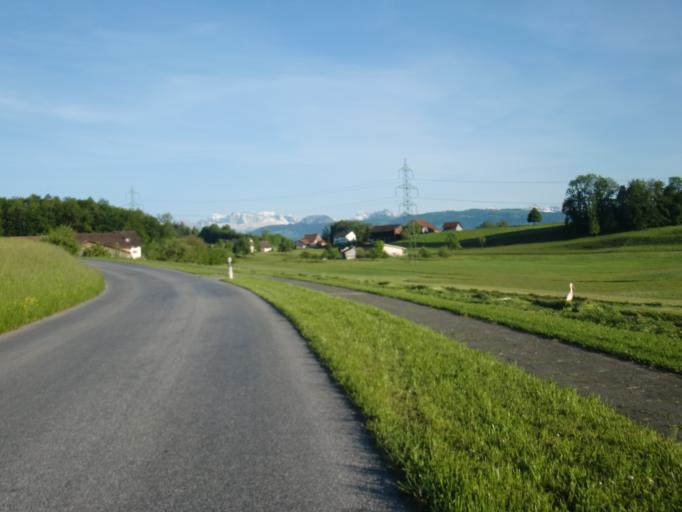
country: CH
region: Zurich
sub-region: Bezirk Hinwil
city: Binzikon
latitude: 47.2741
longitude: 8.7709
